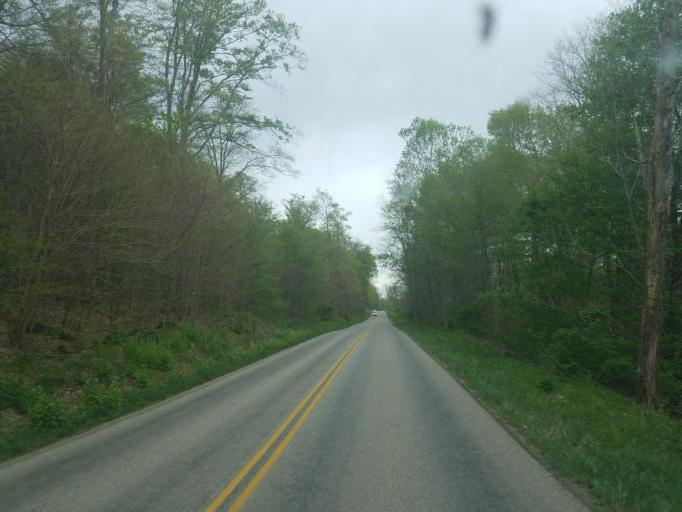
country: US
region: Ohio
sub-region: Richland County
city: Ontario
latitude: 40.7212
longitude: -82.5726
